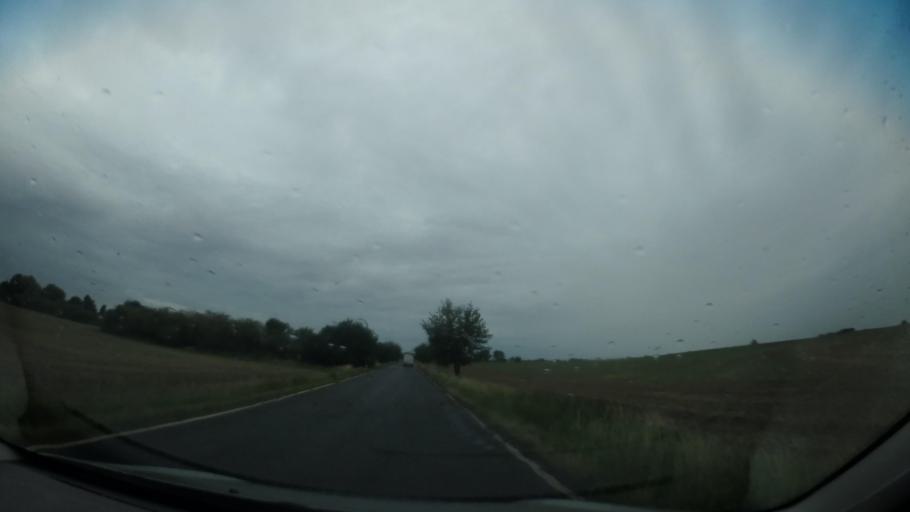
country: CZ
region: Central Bohemia
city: Loucen
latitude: 50.2507
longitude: 15.0220
